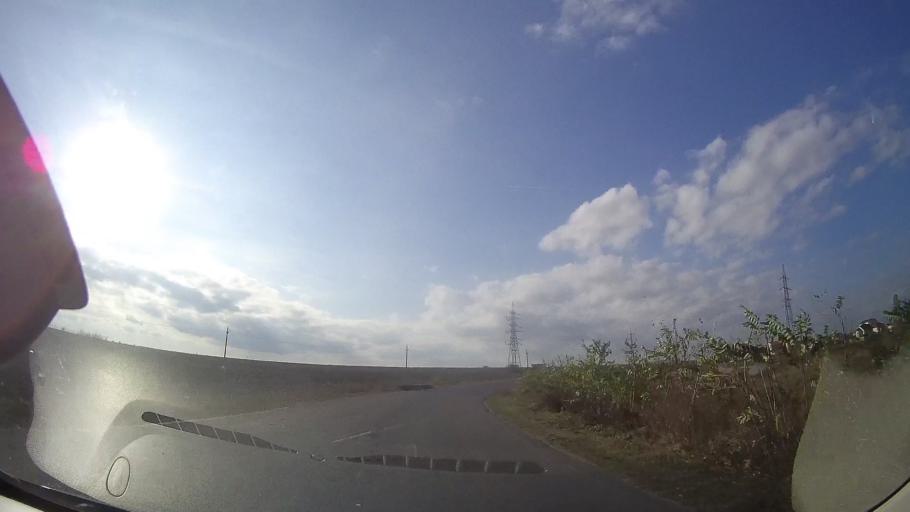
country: RO
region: Constanta
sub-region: Comuna Limanu
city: Limanu
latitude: 43.7908
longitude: 28.5514
